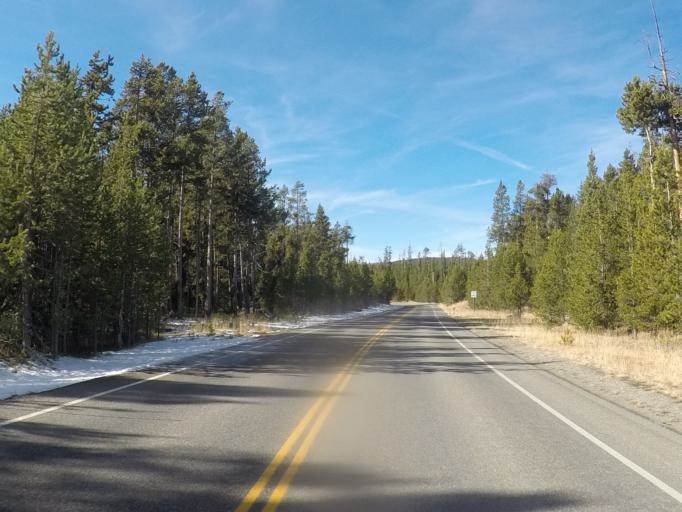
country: US
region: Montana
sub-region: Gallatin County
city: West Yellowstone
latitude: 44.5493
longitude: -110.4130
